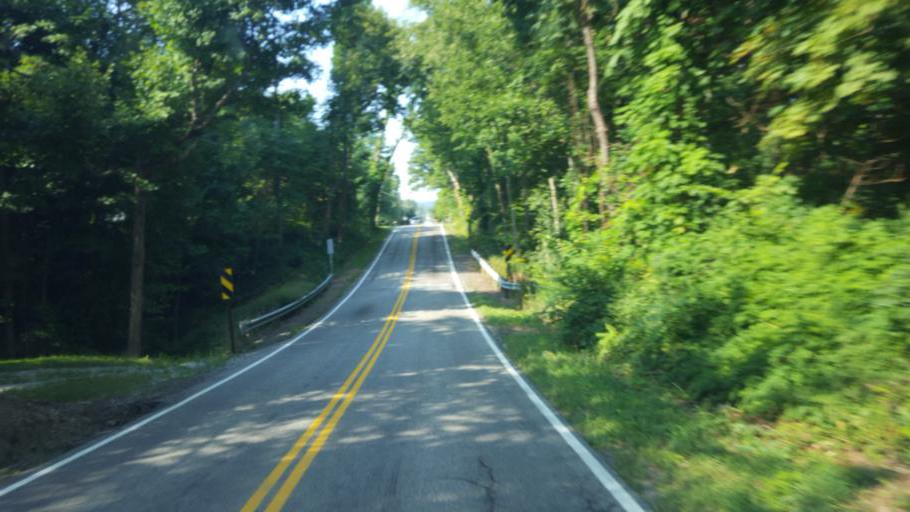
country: US
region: Ohio
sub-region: Lake County
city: Painesville
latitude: 41.6561
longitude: -81.2140
